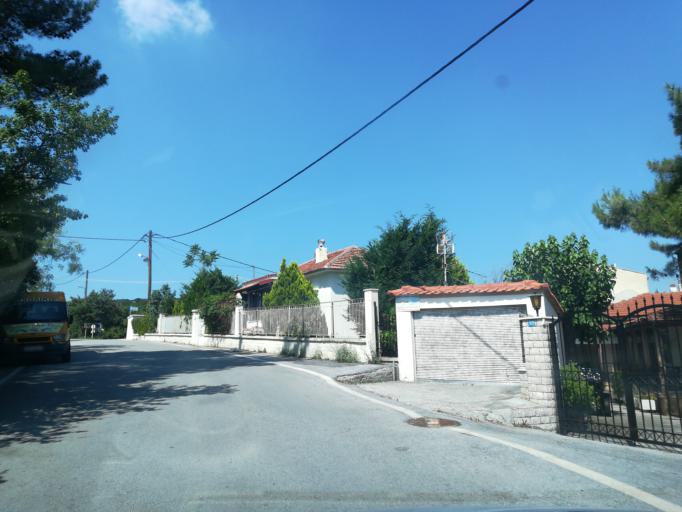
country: GR
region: Central Macedonia
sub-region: Nomos Thessalonikis
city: Asvestochori
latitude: 40.6302
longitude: 23.0400
